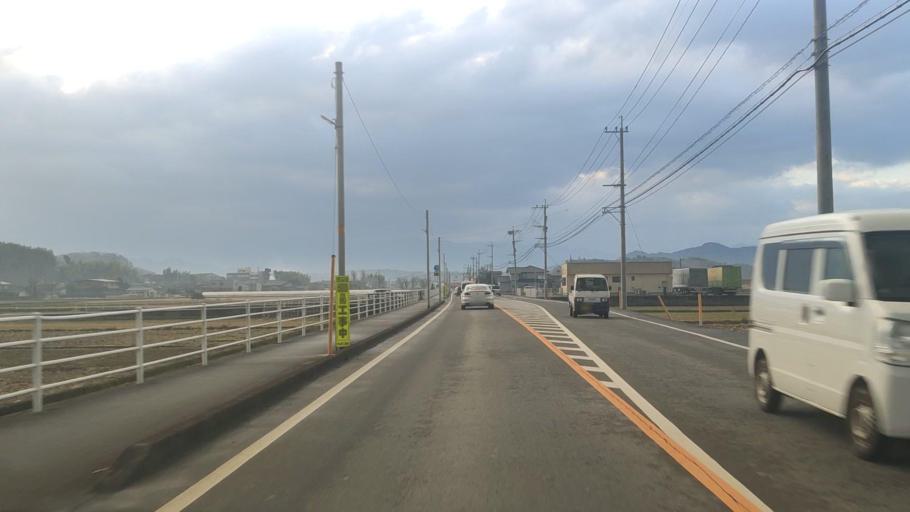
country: JP
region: Kumamoto
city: Uto
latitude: 32.7073
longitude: 130.7766
